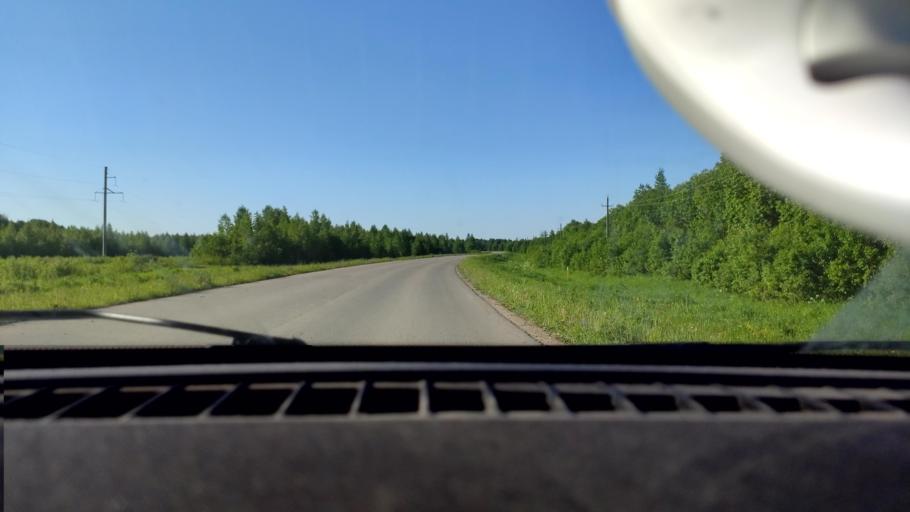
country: RU
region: Perm
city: Polazna
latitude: 58.2048
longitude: 56.5313
